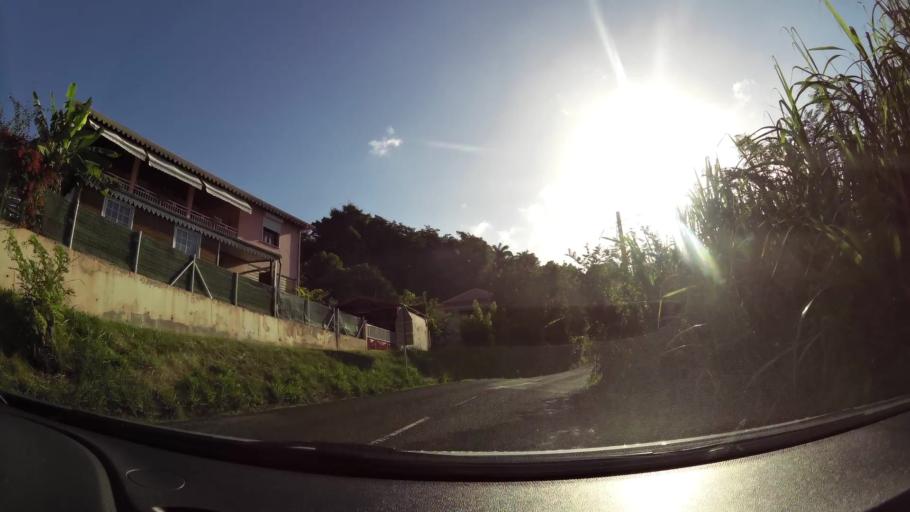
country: MQ
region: Martinique
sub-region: Martinique
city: Le Lamentin
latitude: 14.6340
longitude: -61.0332
